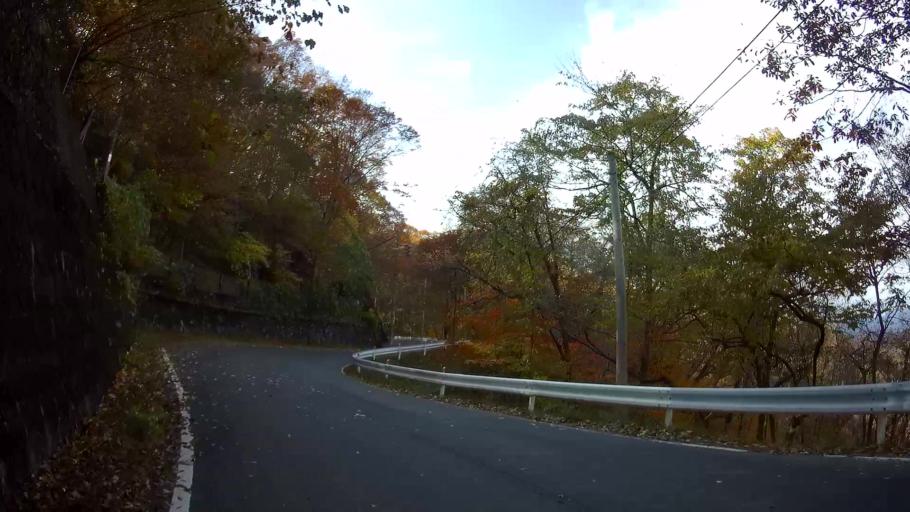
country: JP
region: Gunma
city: Nakanojomachi
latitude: 36.6209
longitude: 138.6342
